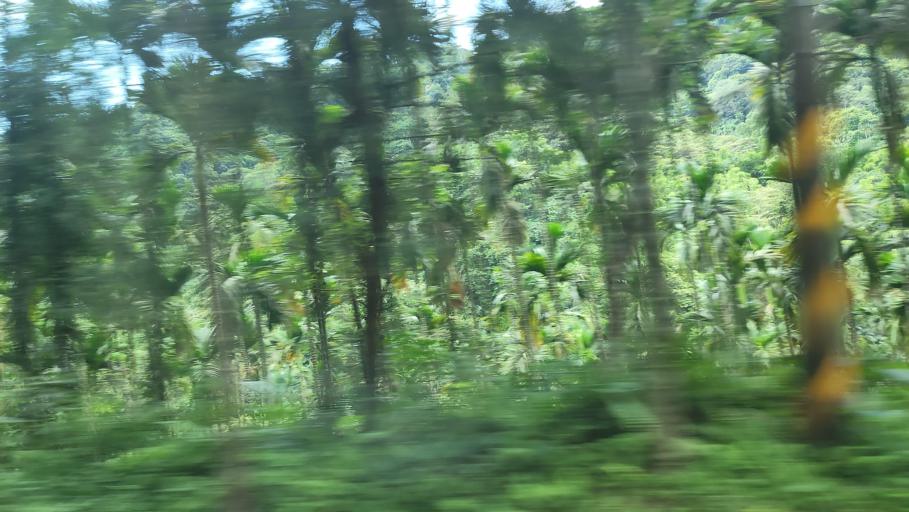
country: TW
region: Taipei
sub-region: Taipei
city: Banqiao
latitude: 24.8976
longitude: 121.4276
